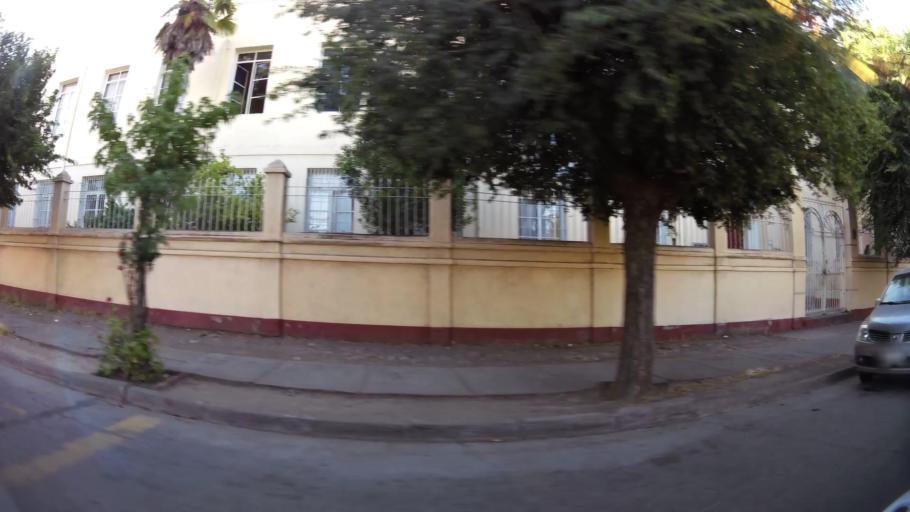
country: CL
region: O'Higgins
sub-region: Provincia de Colchagua
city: Chimbarongo
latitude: -34.5805
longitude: -70.9886
